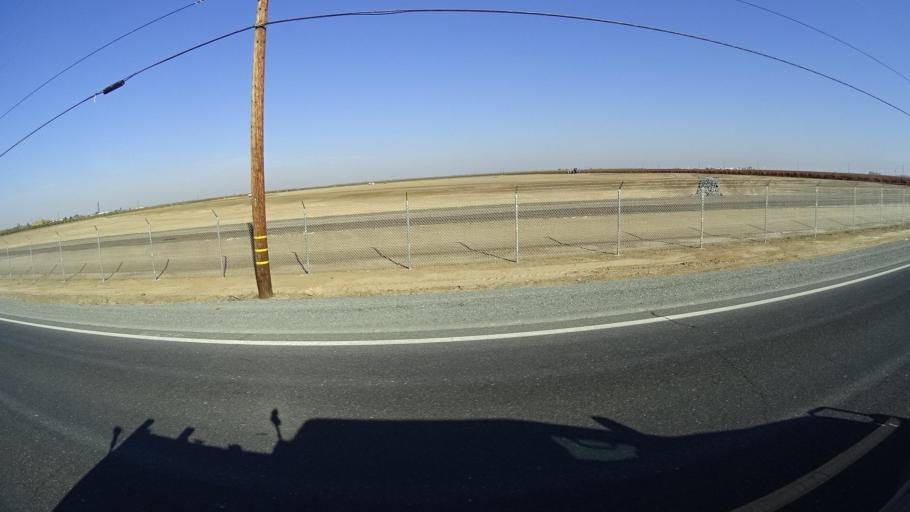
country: US
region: California
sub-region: Kern County
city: Delano
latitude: 35.7614
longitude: -119.2111
